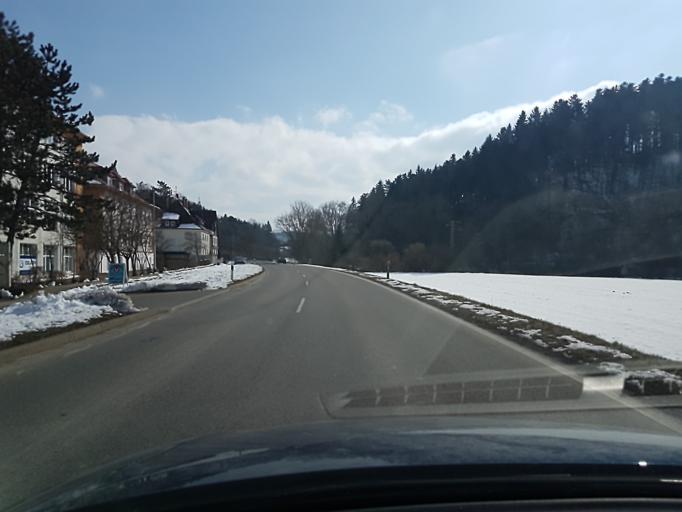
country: DE
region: Baden-Wuerttemberg
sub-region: Freiburg Region
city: Muhlheim am Bach
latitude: 48.3842
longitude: 8.6796
